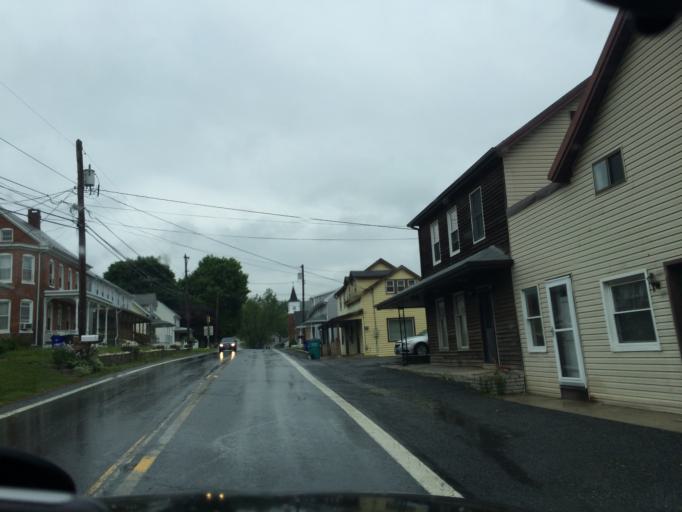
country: US
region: Maryland
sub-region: Washington County
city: Highfield-Cascade
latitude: 39.7004
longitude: -77.4564
